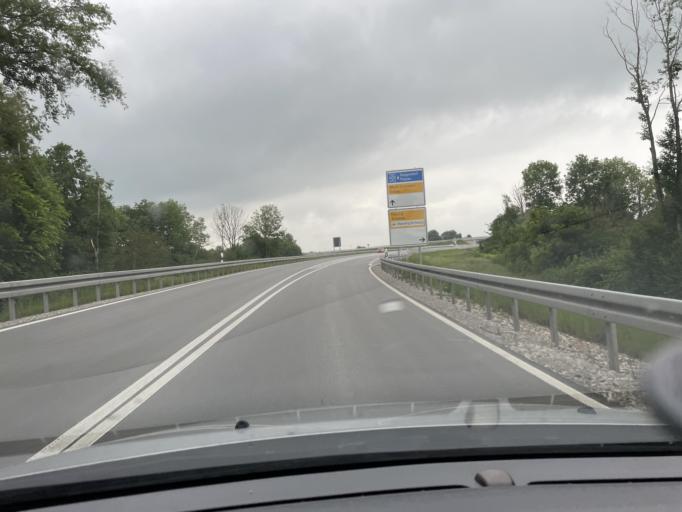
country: DE
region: Bavaria
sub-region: Upper Bavaria
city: Oberding
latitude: 48.3624
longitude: 11.8298
